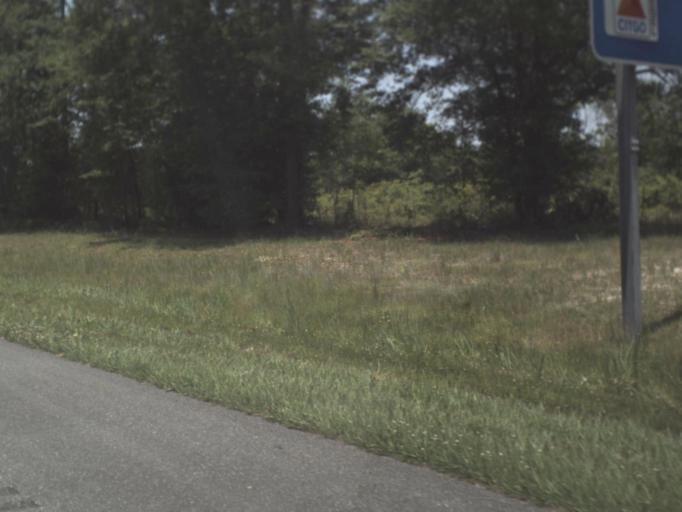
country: US
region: Florida
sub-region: Baker County
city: Macclenny
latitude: 30.2337
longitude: -82.2937
